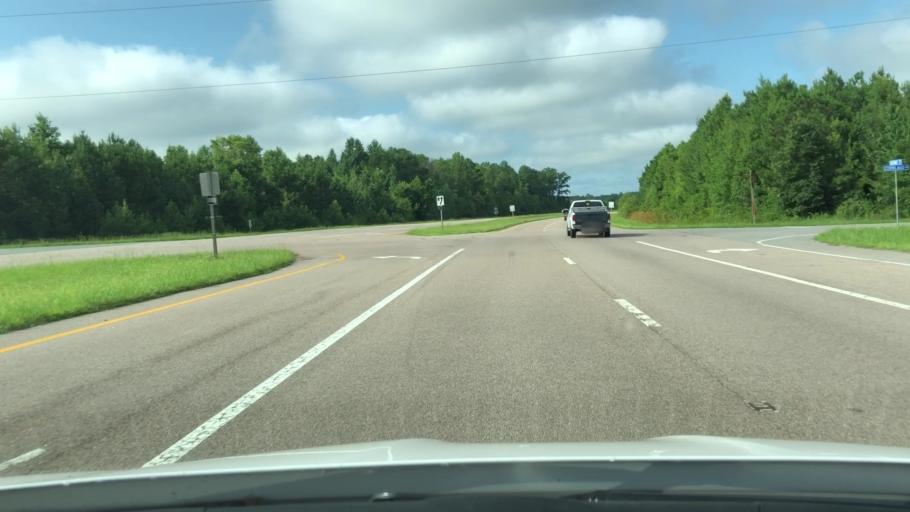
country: US
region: Virginia
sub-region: City of Portsmouth
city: Portsmouth Heights
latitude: 36.6499
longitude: -76.3555
